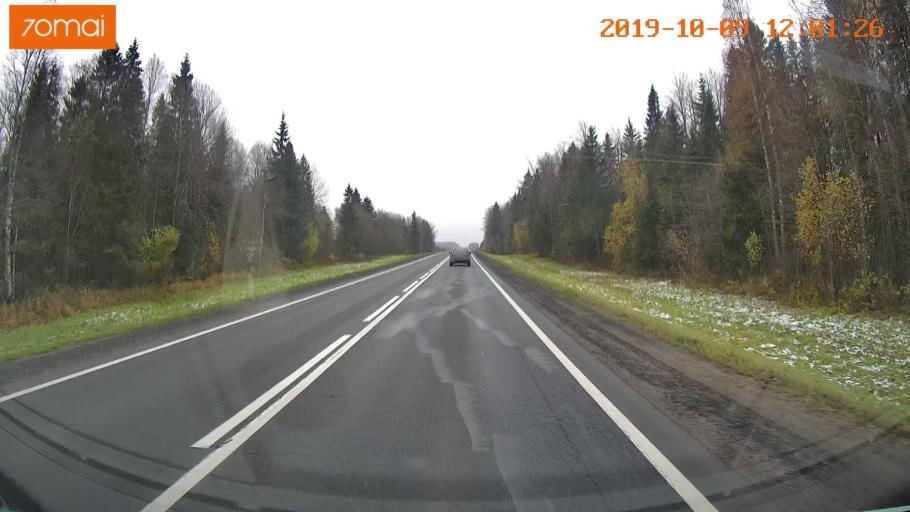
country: RU
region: Vologda
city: Gryazovets
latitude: 58.6881
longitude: 40.3035
